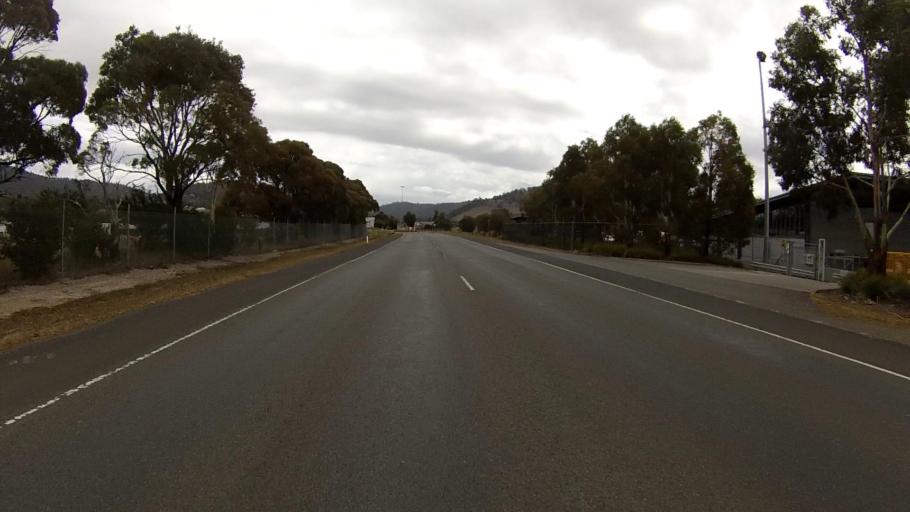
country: AU
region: Tasmania
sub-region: Clarence
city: Cambridge
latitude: -42.8308
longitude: 147.4673
